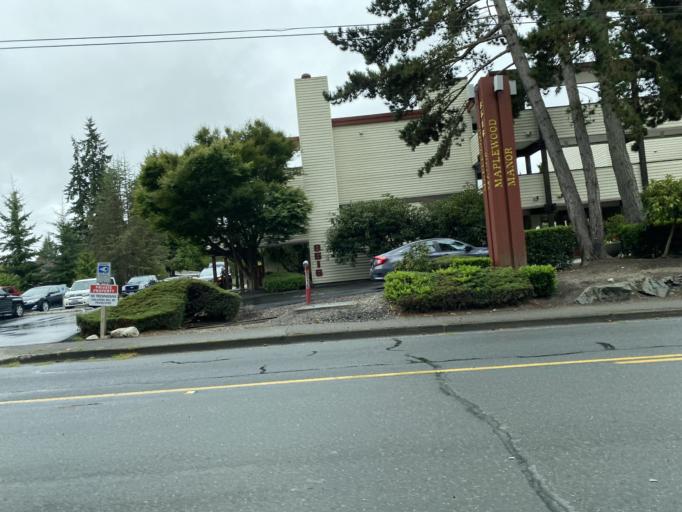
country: US
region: Washington
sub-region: Snohomish County
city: Edmonds
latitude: 47.8215
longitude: -122.3482
